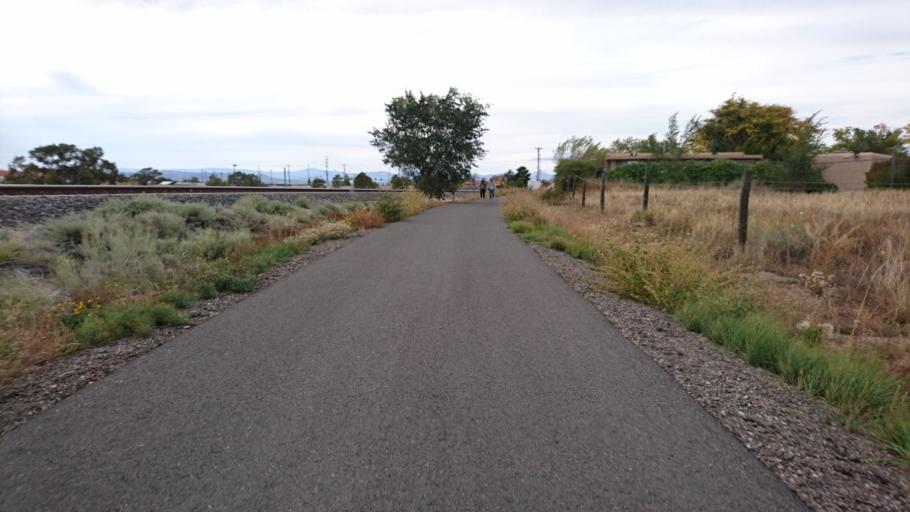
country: US
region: New Mexico
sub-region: Santa Fe County
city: Santa Fe
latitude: 35.6511
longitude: -105.9644
